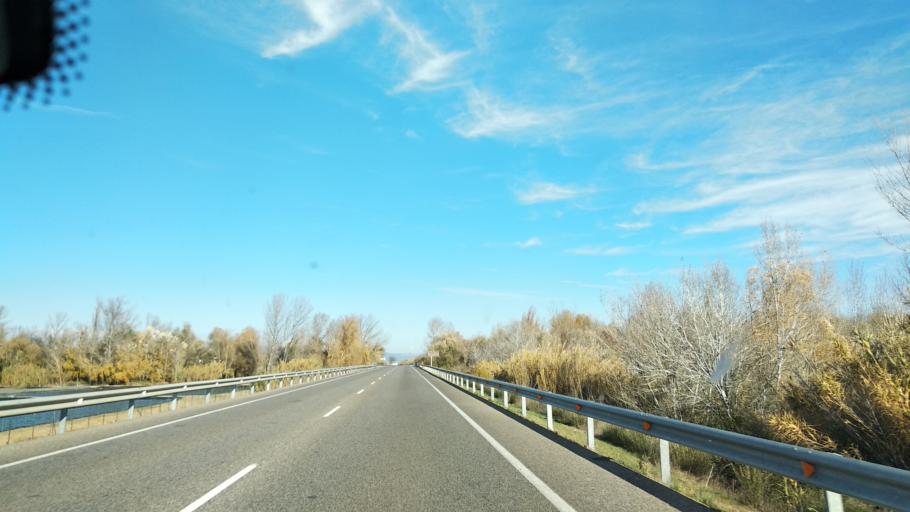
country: ES
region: Catalonia
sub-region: Provincia de Lleida
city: Corbins
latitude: 41.6868
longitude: 0.7012
